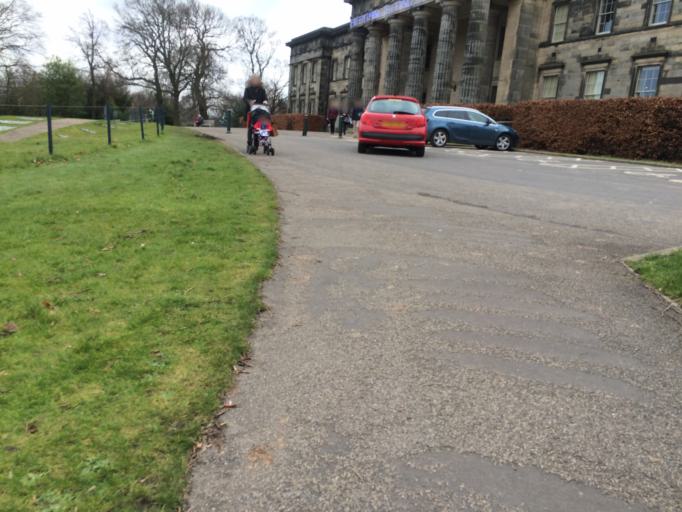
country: GB
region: Scotland
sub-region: Edinburgh
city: Edinburgh
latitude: 55.9513
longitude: -3.2276
